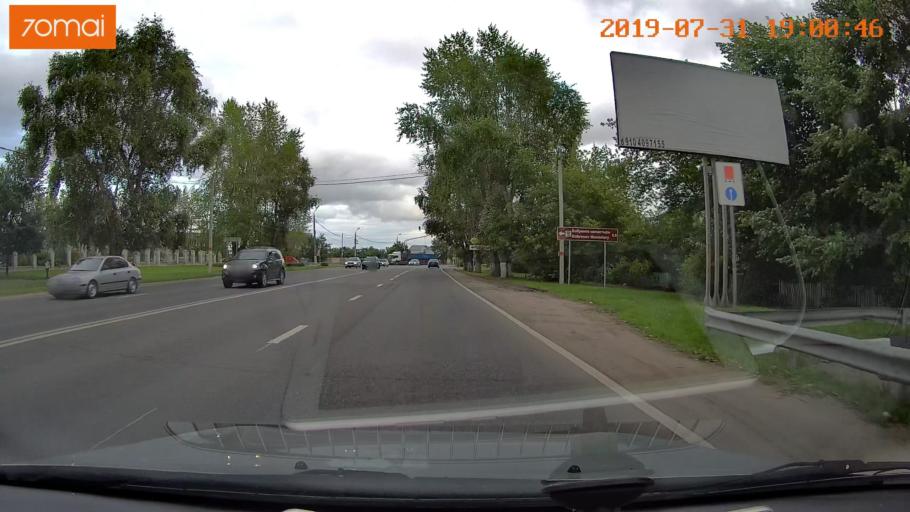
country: RU
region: Moskovskaya
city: Raduzhnyy
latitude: 55.1313
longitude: 38.7268
